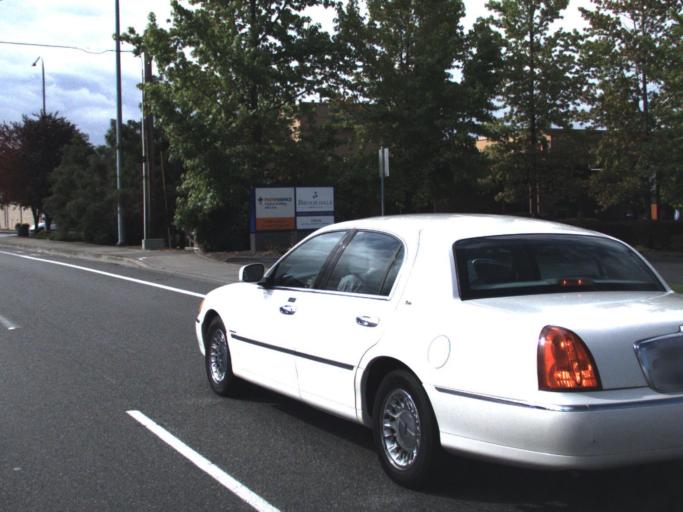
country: US
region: Washington
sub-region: Snohomish County
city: Mill Creek
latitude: 47.8809
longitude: -122.2068
